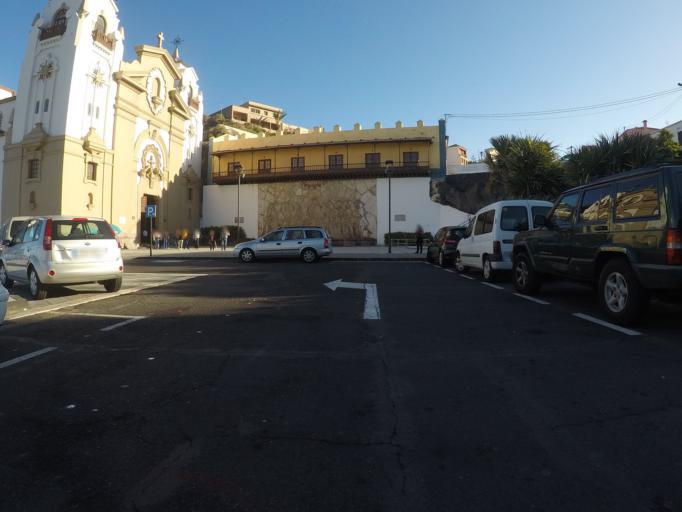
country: ES
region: Canary Islands
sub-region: Provincia de Santa Cruz de Tenerife
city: Candelaria
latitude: 28.3517
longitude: -16.3703
